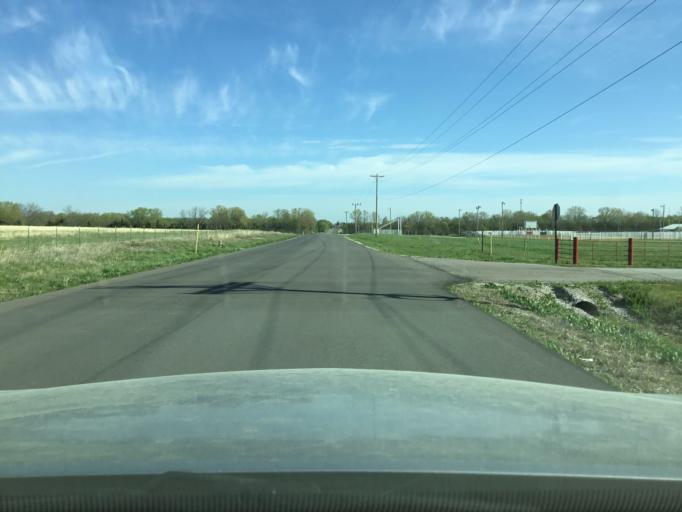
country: US
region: Kansas
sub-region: Neosho County
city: Chanute
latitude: 37.6531
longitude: -95.4435
